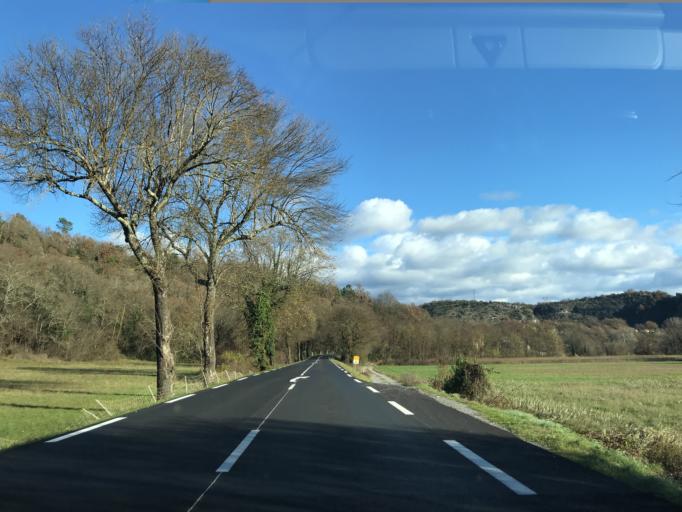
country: FR
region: Rhone-Alpes
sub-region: Departement de l'Ardeche
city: Les Vans
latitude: 44.4158
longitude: 4.1664
